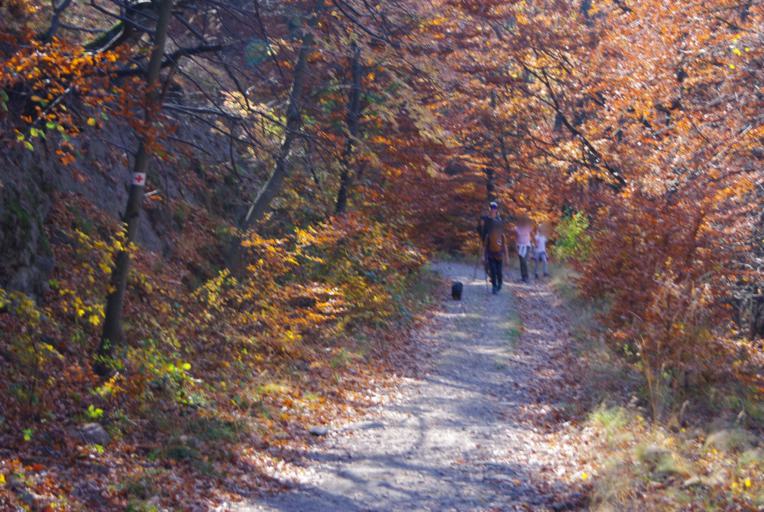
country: HU
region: Pest
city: Pilisszentkereszt
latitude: 47.7383
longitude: 18.9282
